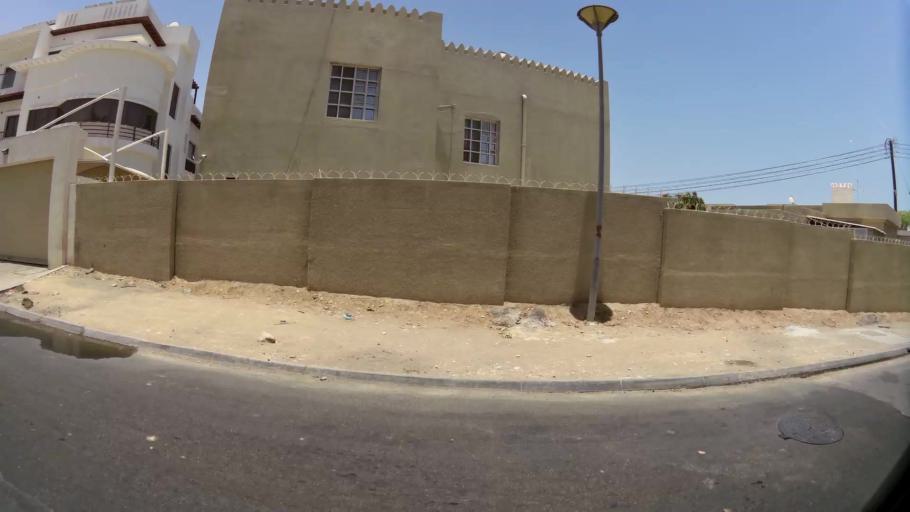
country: OM
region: Muhafazat Masqat
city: Bawshar
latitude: 23.6034
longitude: 58.4530
